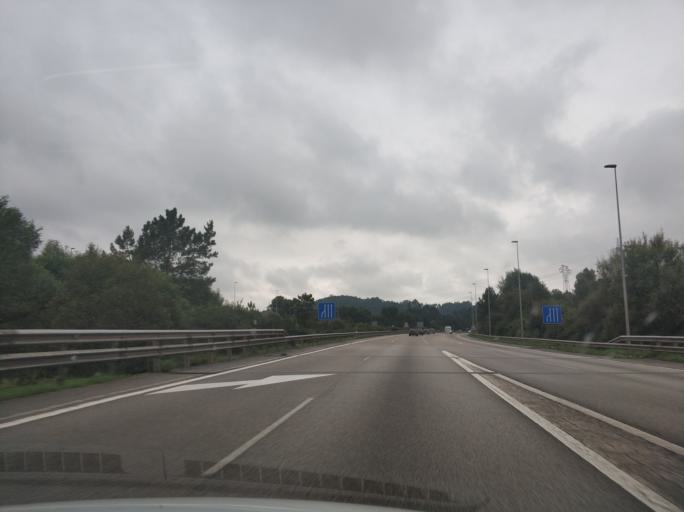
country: ES
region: Asturias
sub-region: Province of Asturias
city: Corvera de Asturias
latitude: 43.5028
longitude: -5.7947
